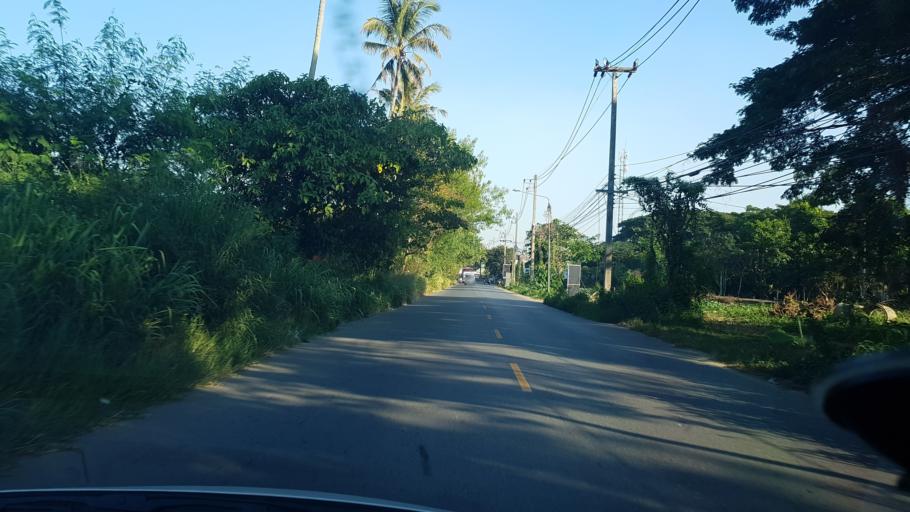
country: TH
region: Chiang Rai
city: Chiang Rai
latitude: 19.9297
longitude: 99.8267
